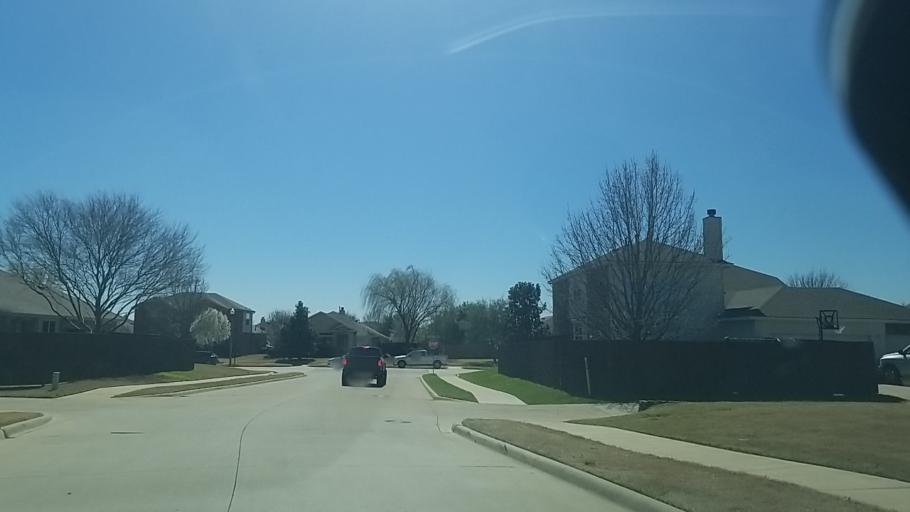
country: US
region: Texas
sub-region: Denton County
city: Corinth
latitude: 33.1557
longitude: -97.1105
